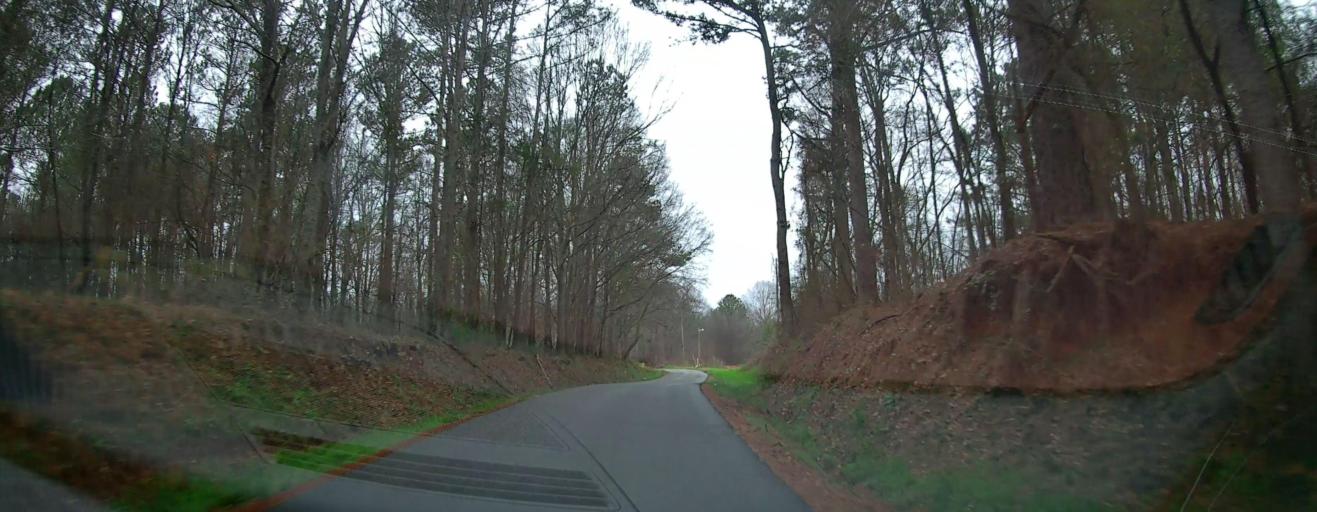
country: US
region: Georgia
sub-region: Monroe County
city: Forsyth
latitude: 33.0510
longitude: -83.8851
